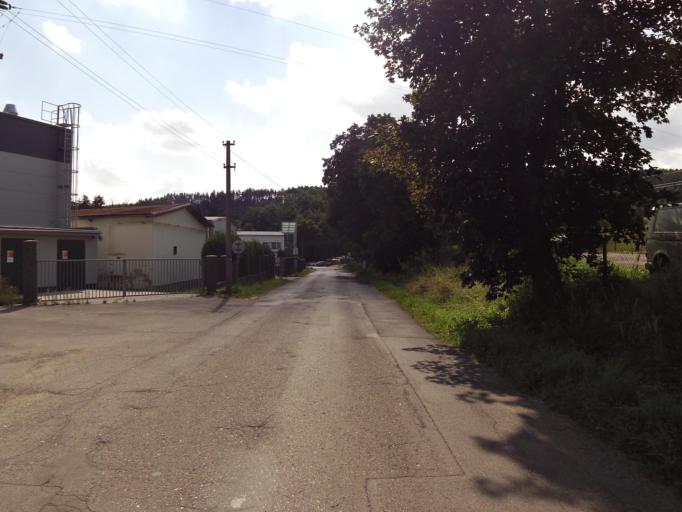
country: CZ
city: Cesky Dub
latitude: 50.6564
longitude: 14.9920
